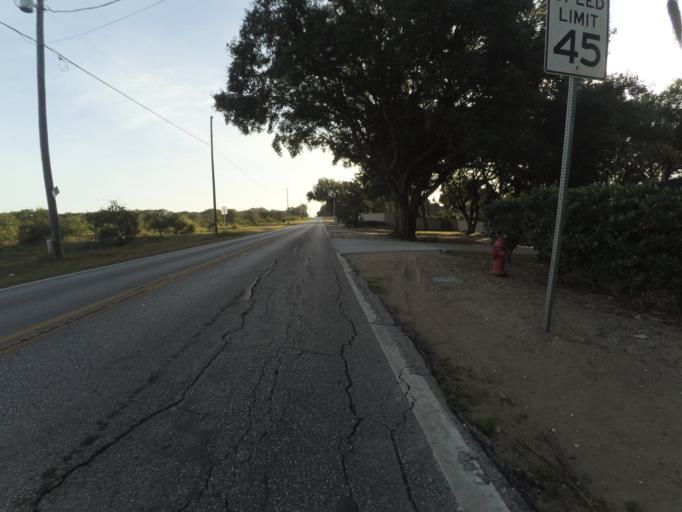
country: US
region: Florida
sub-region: Lake County
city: Umatilla
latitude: 28.9349
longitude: -81.6545
